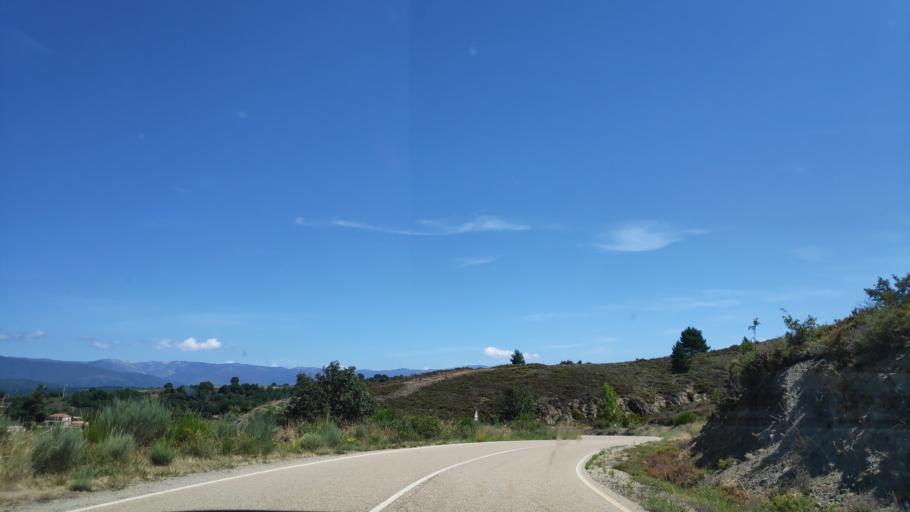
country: ES
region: Castille and Leon
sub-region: Provincia de Zamora
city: Requejo
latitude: 42.0212
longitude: -6.6977
